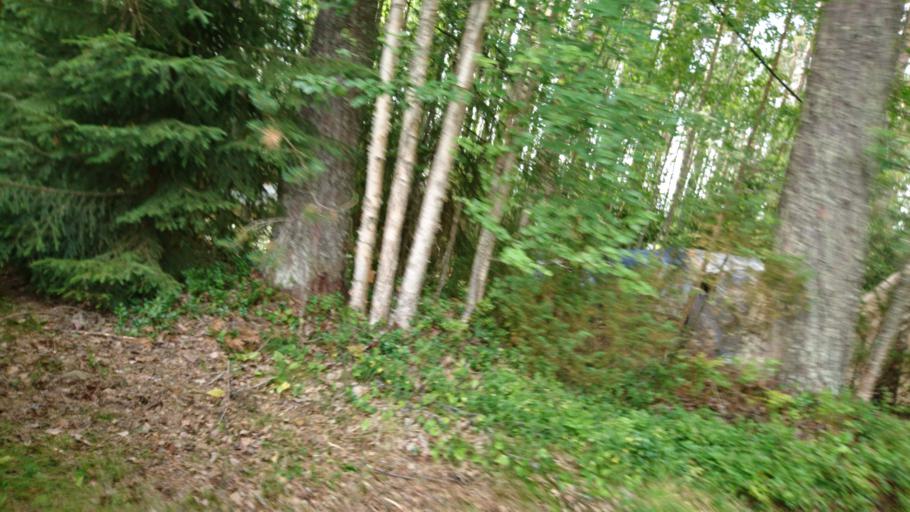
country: SE
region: Vaesternorrland
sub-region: Solleftea Kommun
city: As
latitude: 63.4441
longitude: 16.8846
